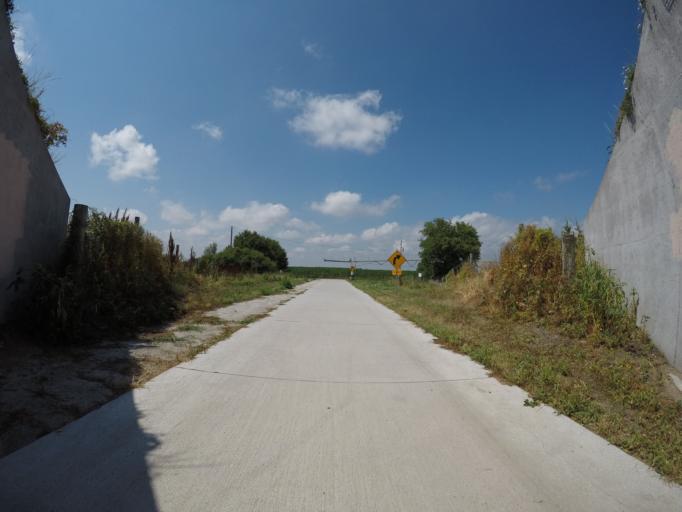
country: US
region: Nebraska
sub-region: Buffalo County
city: Kearney
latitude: 40.6793
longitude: -98.9927
